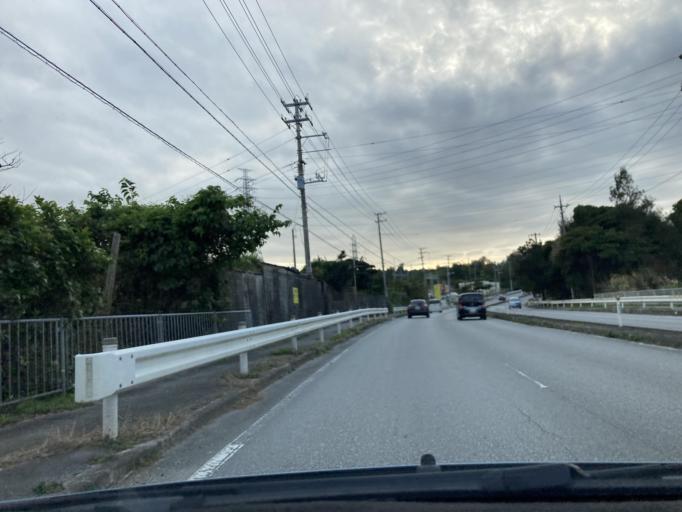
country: JP
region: Okinawa
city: Ishikawa
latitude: 26.4336
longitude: 127.8177
